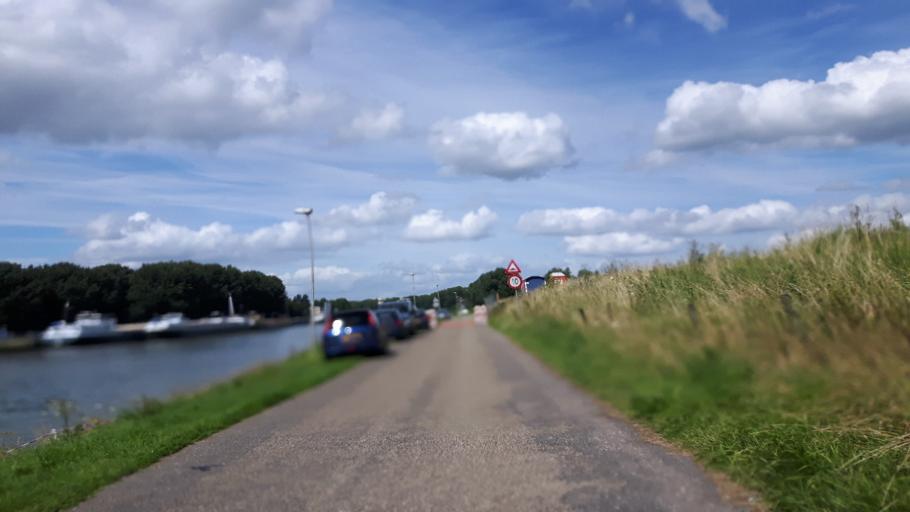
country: NL
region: Utrecht
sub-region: Gemeente Vianen
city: Vianen
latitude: 52.0174
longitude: 5.1119
